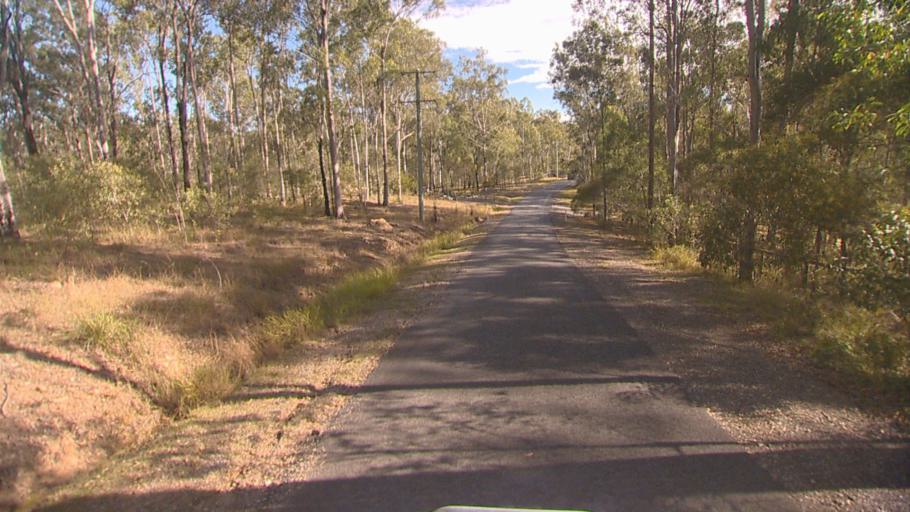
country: AU
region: Queensland
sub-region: Logan
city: Cedar Vale
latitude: -27.8359
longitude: 153.0713
